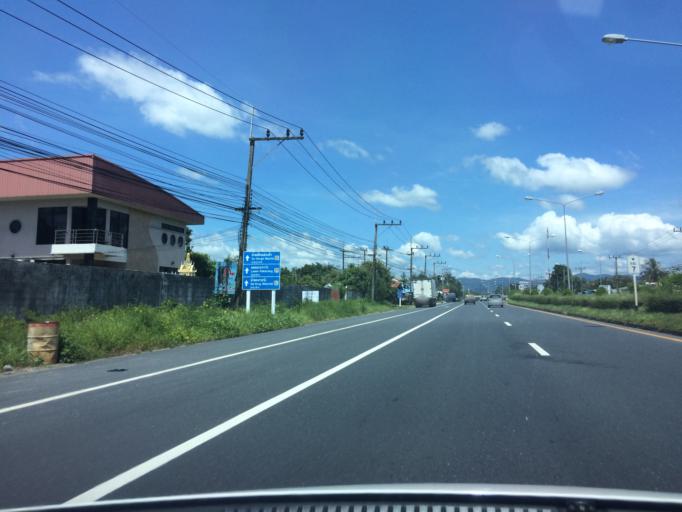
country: TH
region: Phangnga
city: Thai Mueang
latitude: 8.2164
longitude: 98.2970
